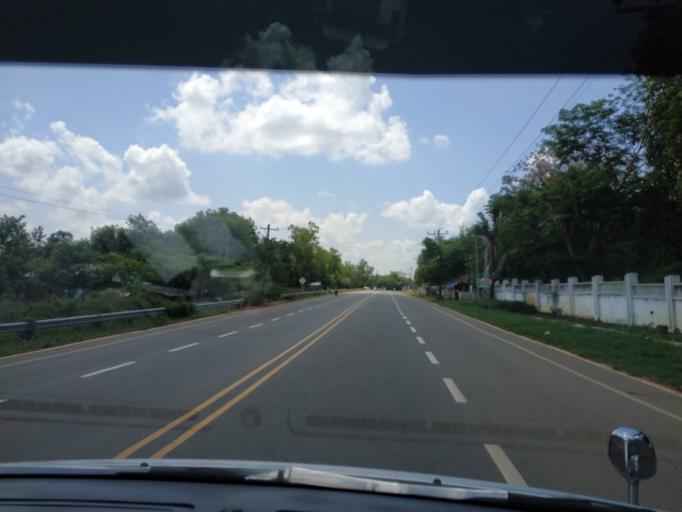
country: MM
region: Mon
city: Kyaikto
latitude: 17.3382
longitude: 97.0395
